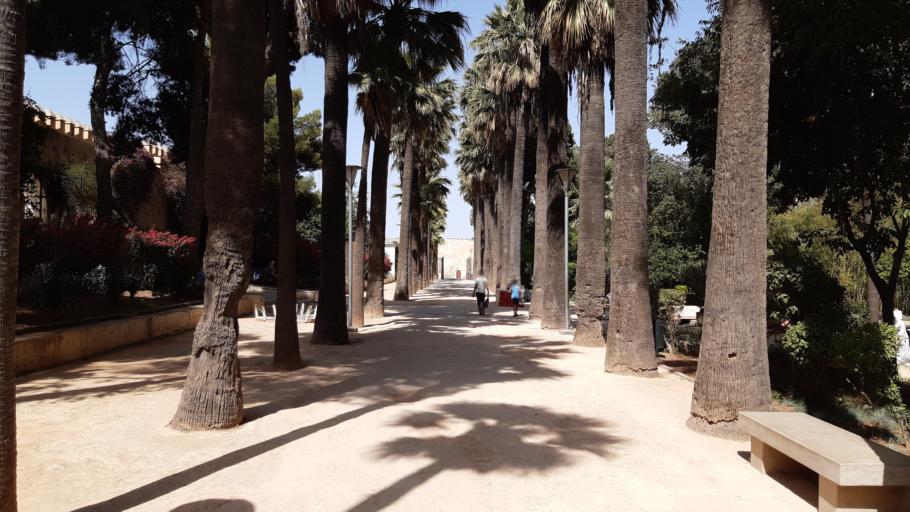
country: MA
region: Fes-Boulemane
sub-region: Fes
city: Fes
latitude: 34.0592
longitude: -4.9892
